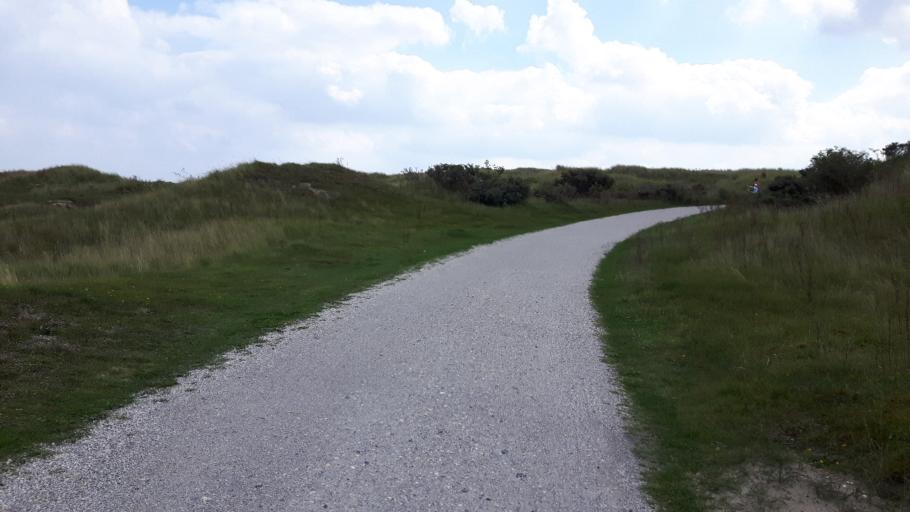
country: NL
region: Friesland
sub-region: Gemeente Dongeradeel
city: Holwerd
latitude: 53.4615
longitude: 5.8997
